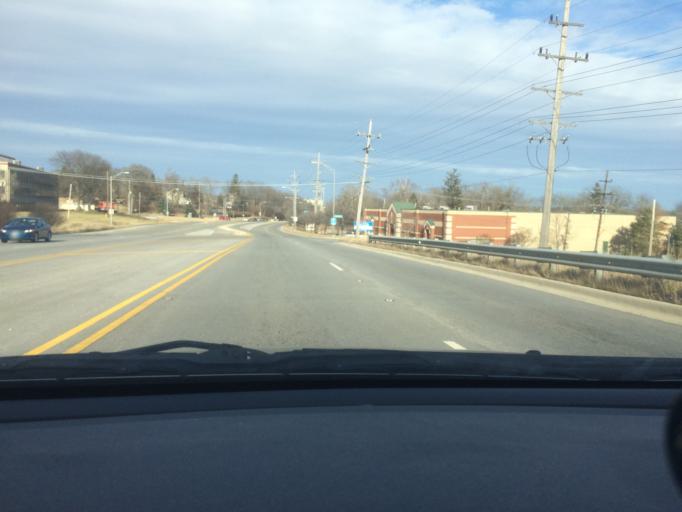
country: US
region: Illinois
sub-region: Kane County
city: Elgin
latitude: 42.0559
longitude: -88.2949
